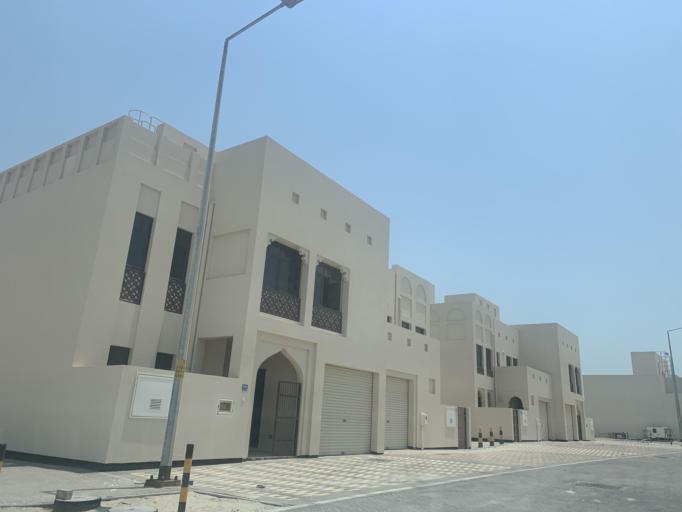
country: BH
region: Muharraq
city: Al Hadd
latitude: 26.2379
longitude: 50.6694
